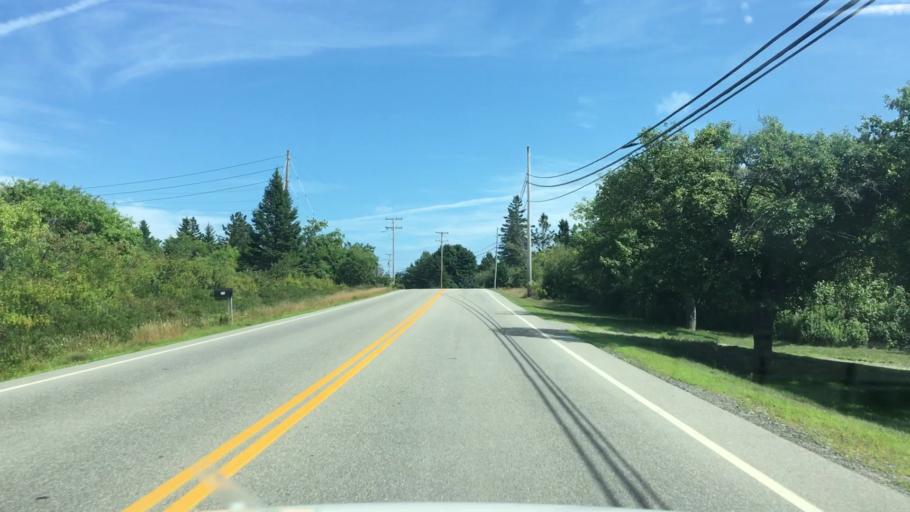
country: US
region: Maine
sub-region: Washington County
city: Eastport
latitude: 44.9134
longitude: -67.0048
